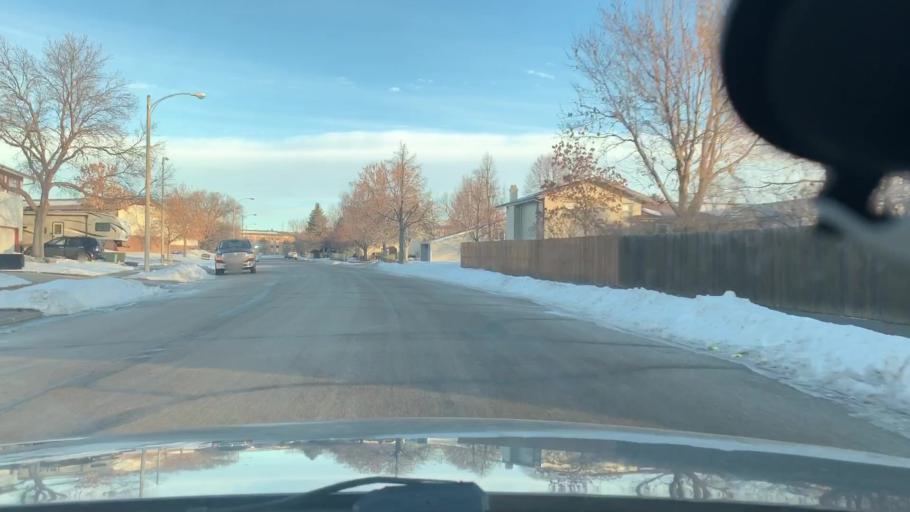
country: US
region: North Dakota
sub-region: Burleigh County
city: Bismarck
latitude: 46.8256
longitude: -100.8066
